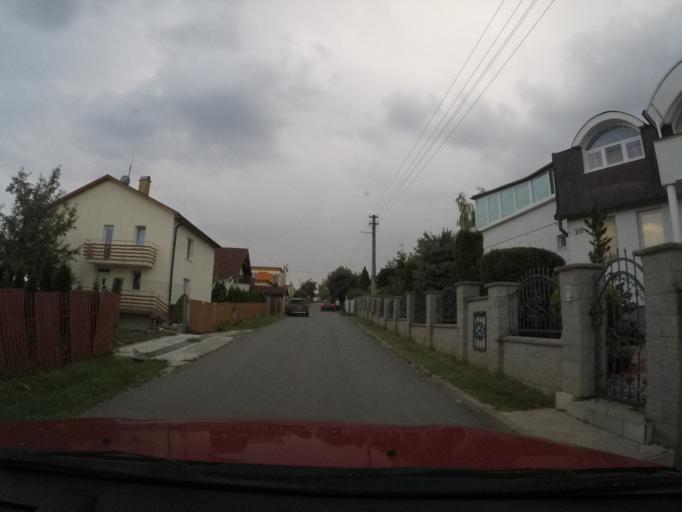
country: SK
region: Kosicky
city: Kosice
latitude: 48.6912
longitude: 21.2072
